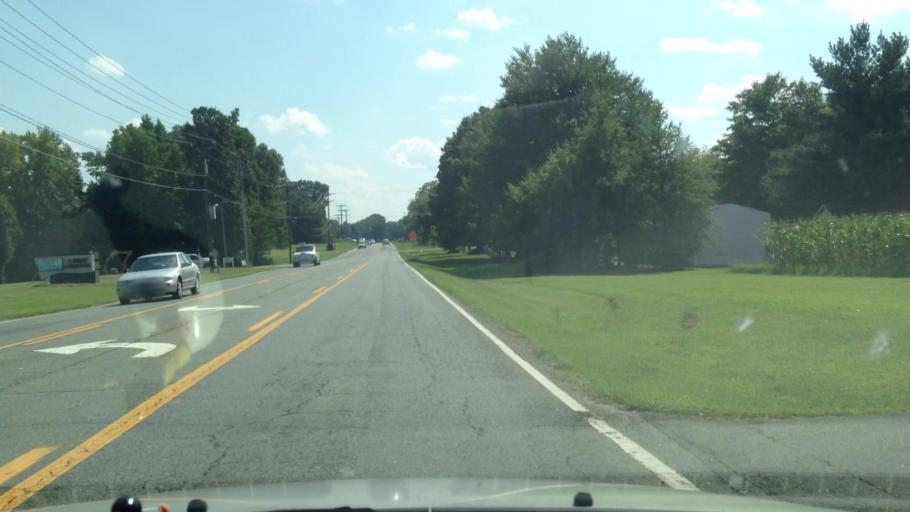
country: US
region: North Carolina
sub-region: Forsyth County
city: Kernersville
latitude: 36.1395
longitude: -80.0504
